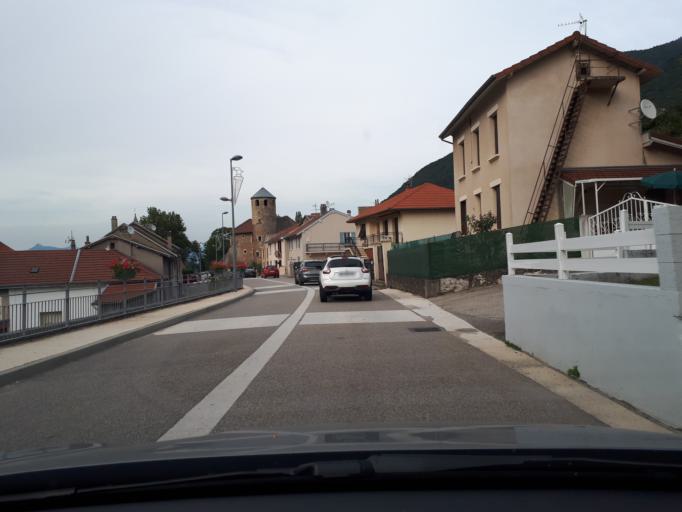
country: FR
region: Rhone-Alpes
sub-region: Departement de l'Isere
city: Saint-Georges-de-Commiers
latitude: 45.0373
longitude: 5.7035
